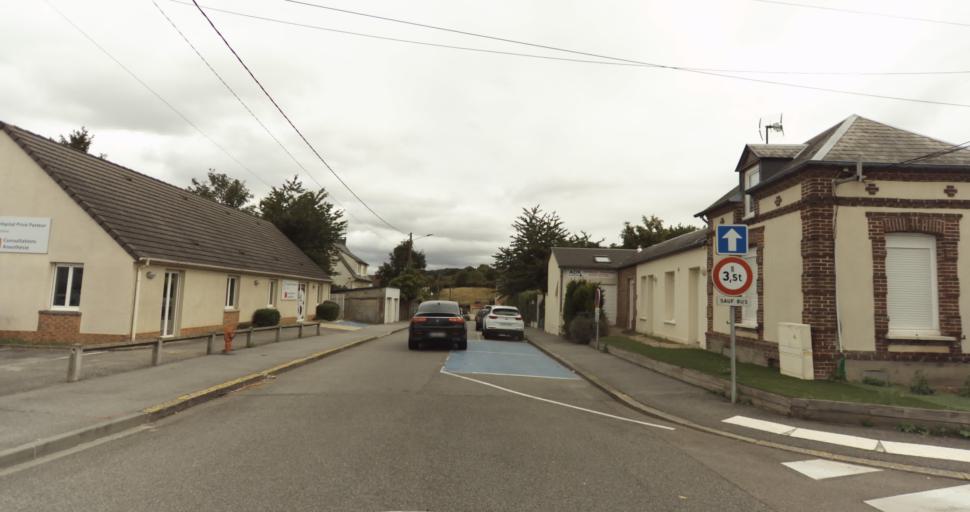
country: FR
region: Haute-Normandie
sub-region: Departement de l'Eure
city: Evreux
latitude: 49.0291
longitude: 1.1608
